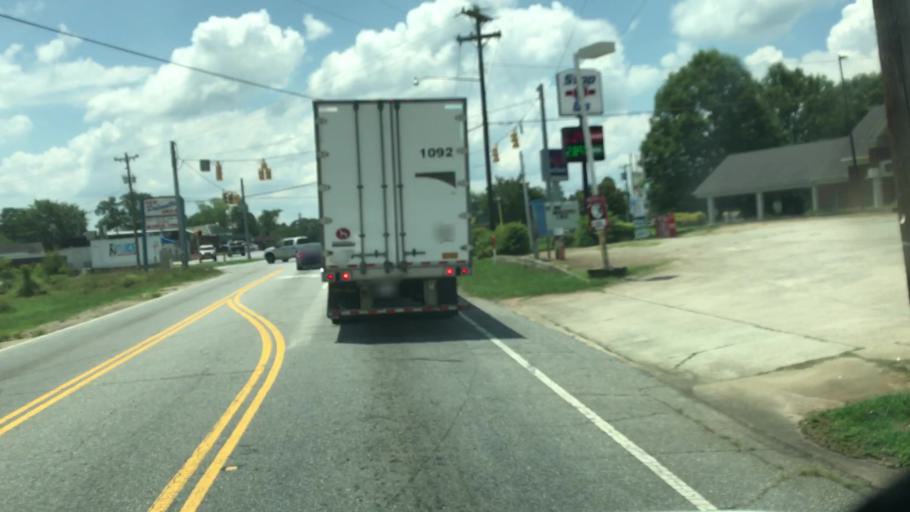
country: US
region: South Carolina
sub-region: Anderson County
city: Williamston
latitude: 34.6230
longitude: -82.4709
